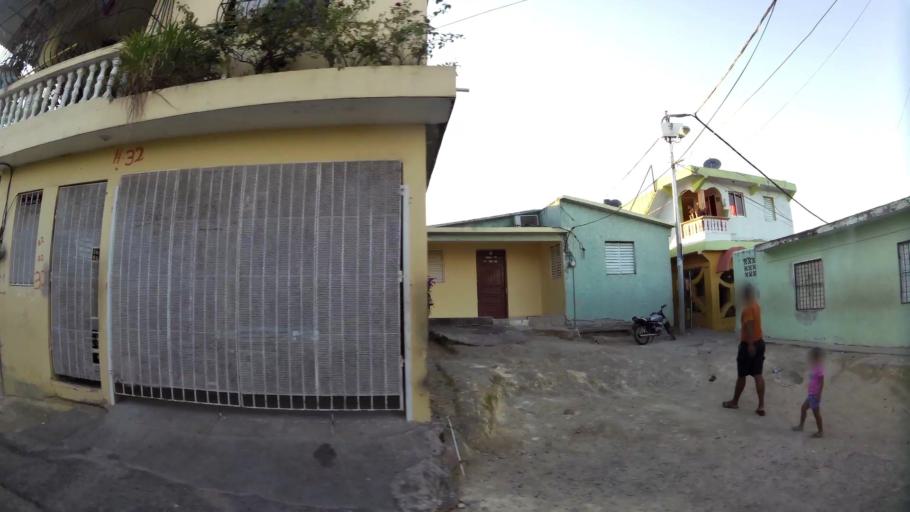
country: DO
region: Nacional
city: Santo Domingo
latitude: 18.4956
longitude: -69.9633
